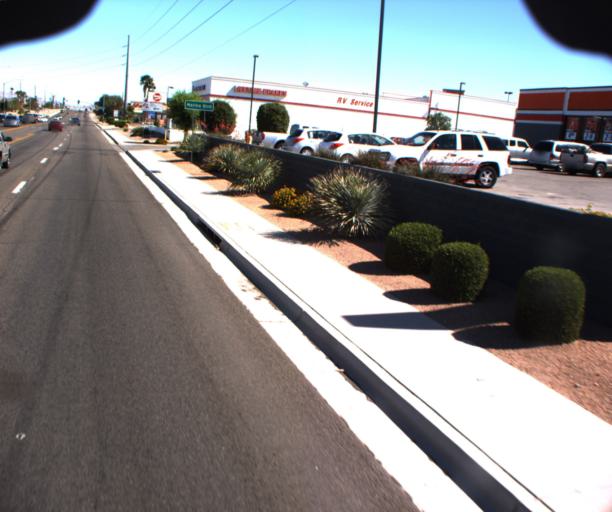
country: US
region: Arizona
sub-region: Mohave County
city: Bullhead City
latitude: 35.0986
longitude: -114.5979
